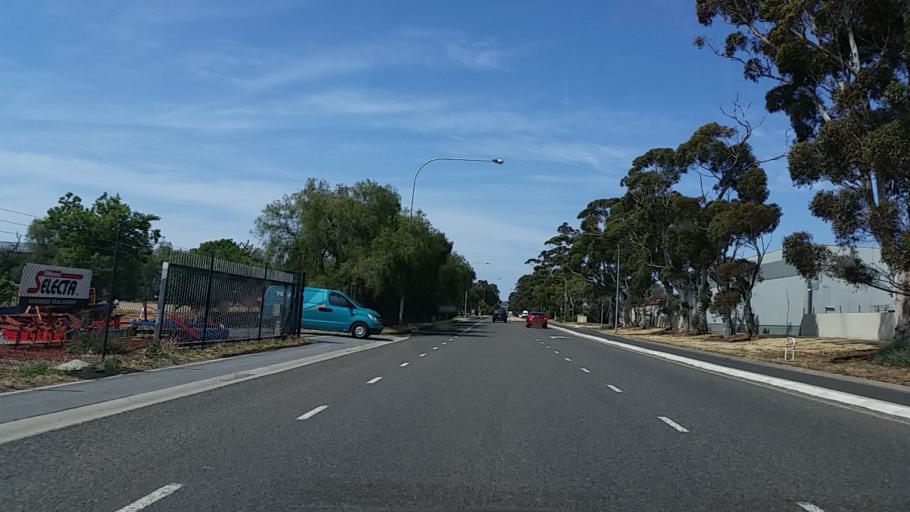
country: AU
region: South Australia
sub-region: Port Adelaide Enfield
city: Enfield
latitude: -34.8308
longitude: 138.6035
